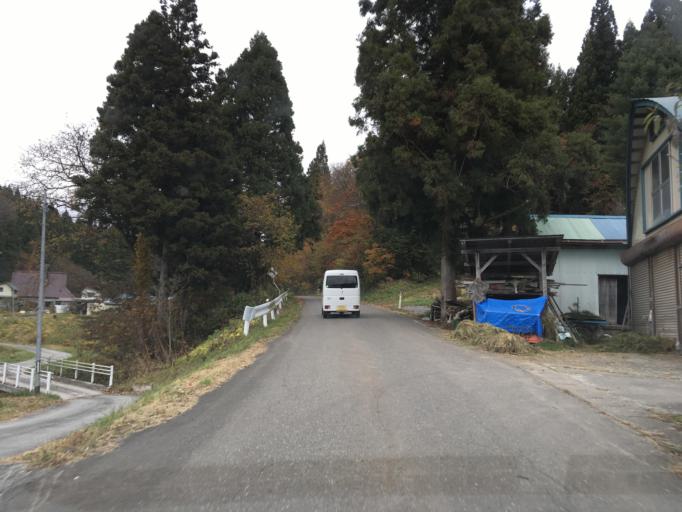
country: JP
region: Iwate
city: Mizusawa
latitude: 39.1131
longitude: 141.3271
